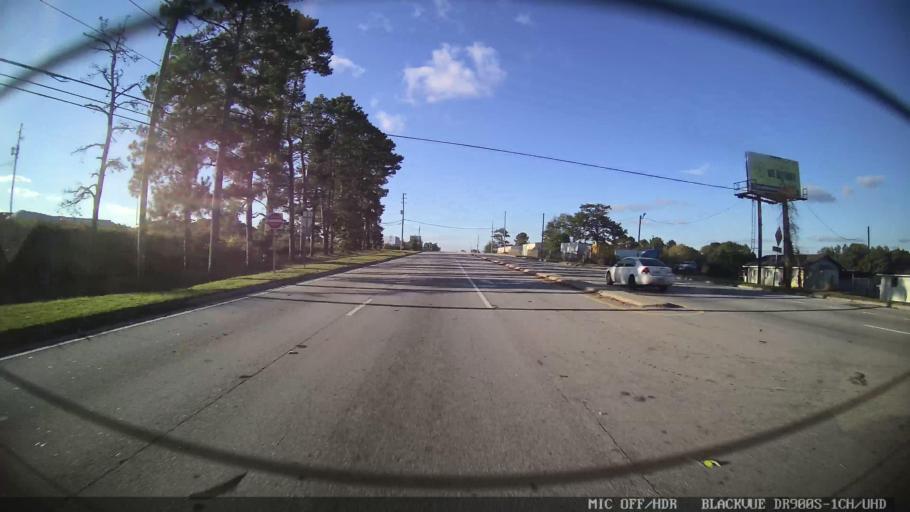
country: US
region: Georgia
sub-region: Clayton County
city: Conley
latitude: 33.6306
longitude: -84.3146
